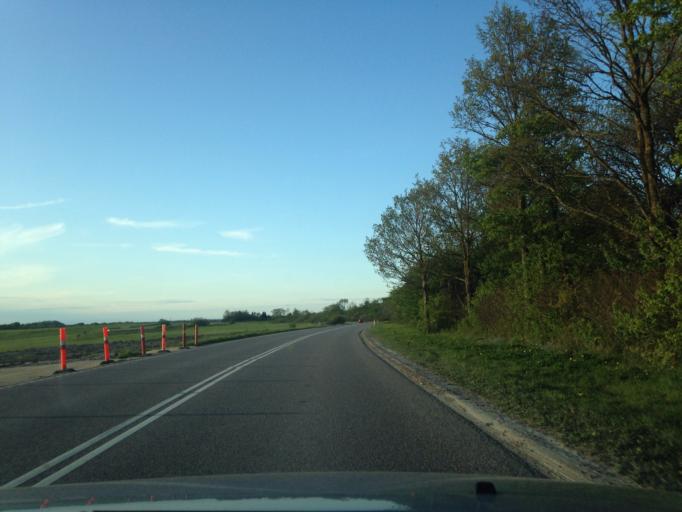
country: DK
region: Zealand
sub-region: Greve Kommune
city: Tune
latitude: 55.6226
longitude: 12.1848
